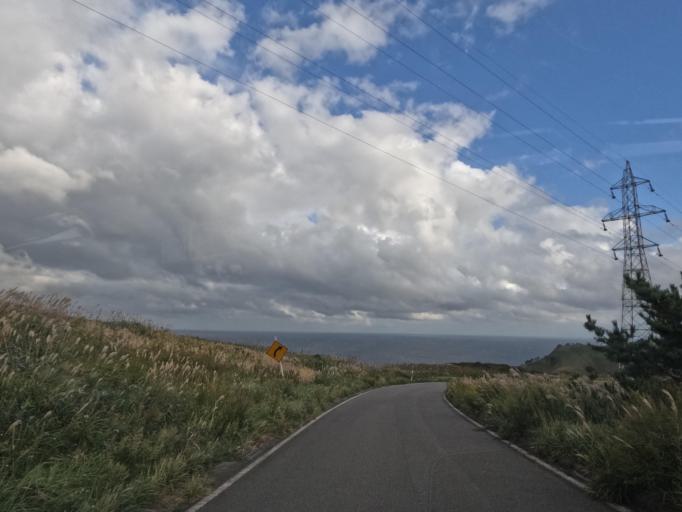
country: JP
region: Hokkaido
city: Muroran
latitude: 42.3140
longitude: 141.0056
